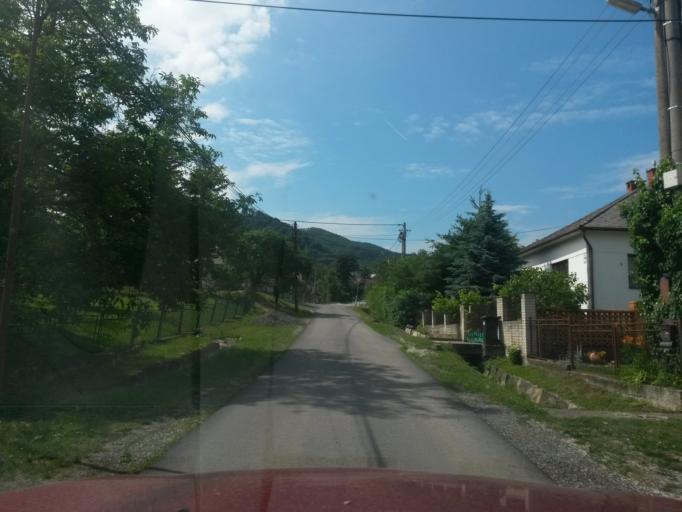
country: SK
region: Kosicky
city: Secovce
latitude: 48.6326
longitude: 21.4822
